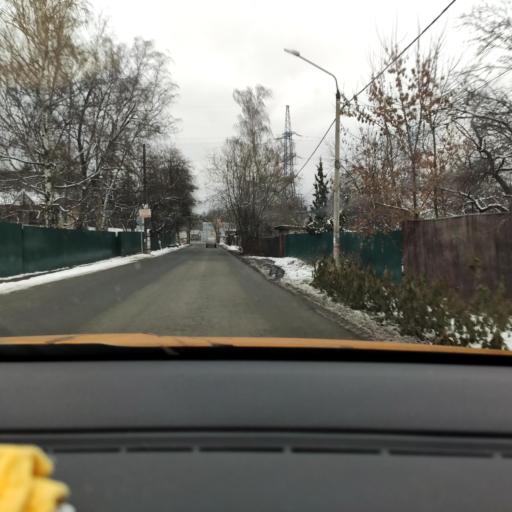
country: RU
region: Moskovskaya
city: Druzhba
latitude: 55.8892
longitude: 37.7445
